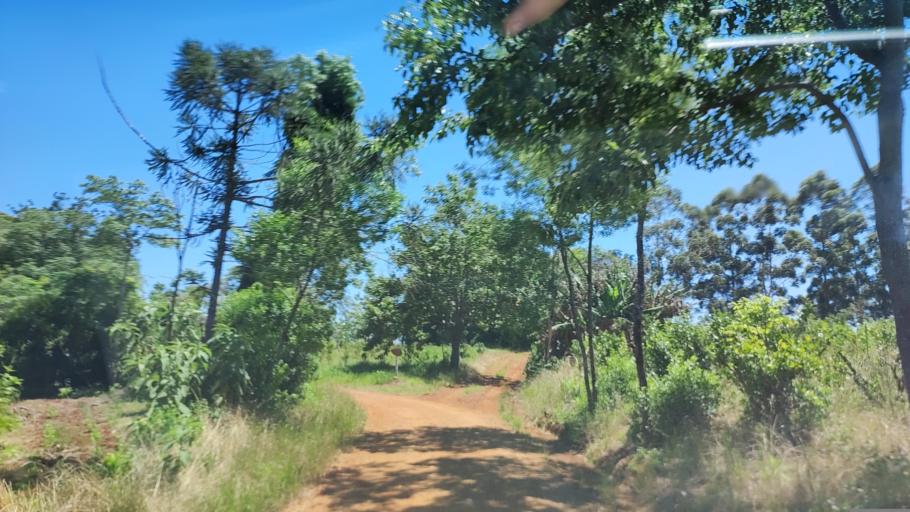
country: AR
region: Misiones
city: Dos de Mayo
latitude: -27.0068
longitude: -54.6223
